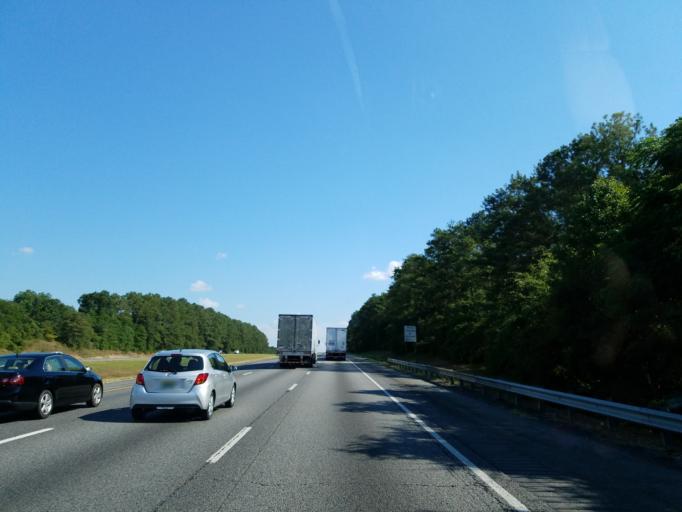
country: US
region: Georgia
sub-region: Houston County
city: Perry
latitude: 32.5277
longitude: -83.7438
